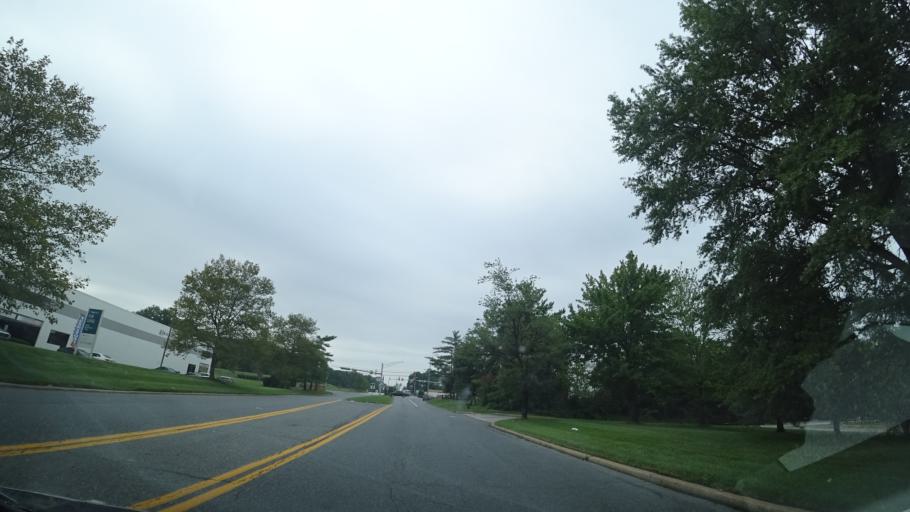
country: US
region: Maryland
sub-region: Howard County
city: Savage
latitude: 39.1502
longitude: -76.8018
